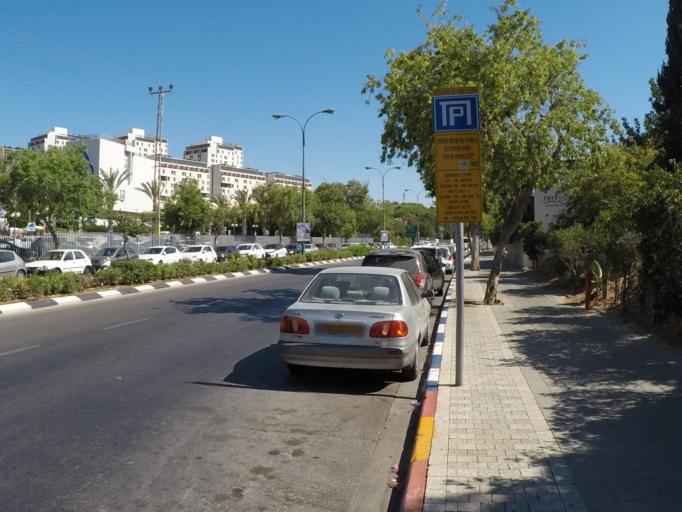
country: IL
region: Tel Aviv
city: Ramat Gan
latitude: 32.1101
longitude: 34.8015
